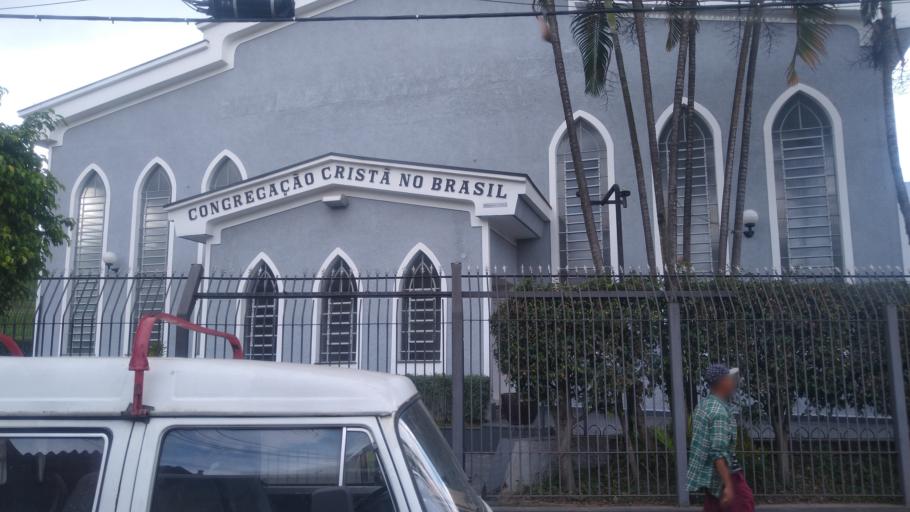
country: BR
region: Sao Paulo
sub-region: Caieiras
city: Caieiras
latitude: -23.4527
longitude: -46.6992
